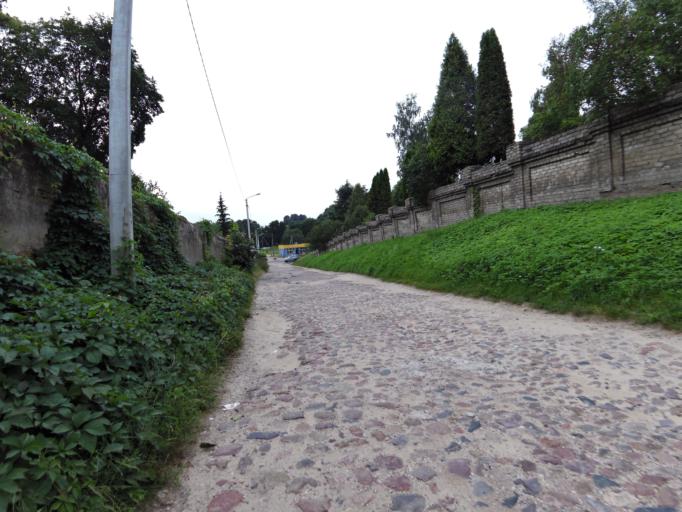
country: LT
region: Vilnius County
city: Rasos
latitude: 54.6655
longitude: 25.2934
